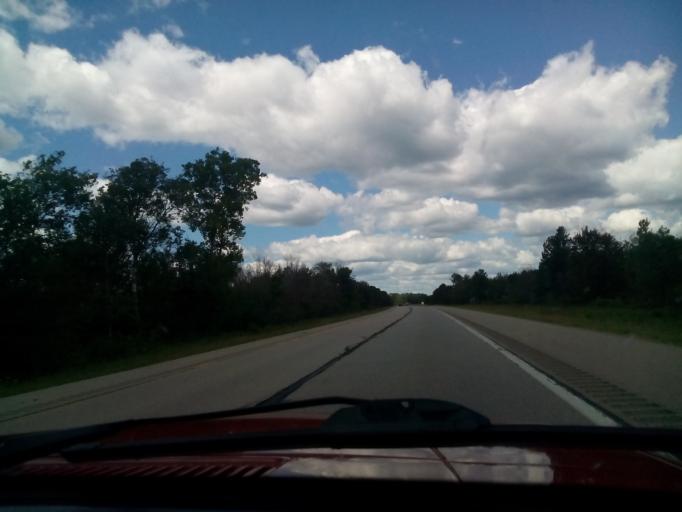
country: US
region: Michigan
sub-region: Ogemaw County
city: Skidway Lake
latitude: 44.0983
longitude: -84.1102
